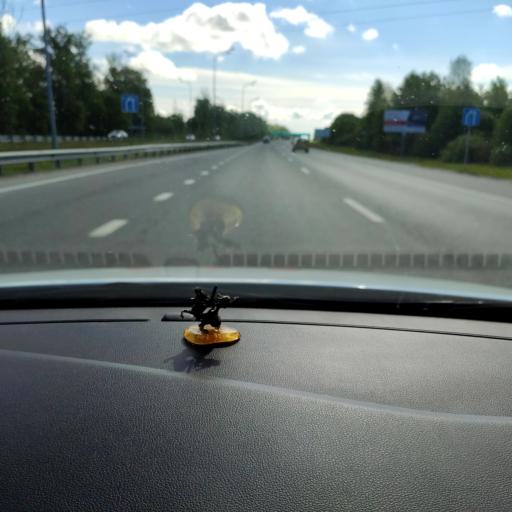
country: RU
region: Tatarstan
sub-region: Zelenodol'skiy Rayon
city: Vasil'yevo
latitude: 55.8720
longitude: 48.7075
